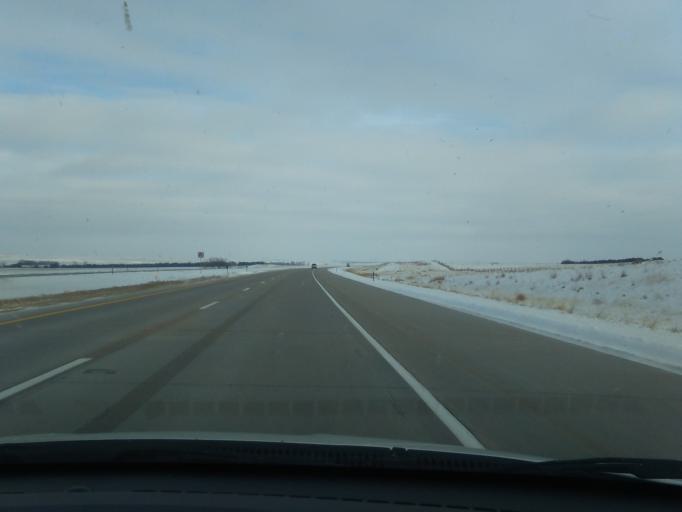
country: US
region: Nebraska
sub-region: Deuel County
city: Chappell
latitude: 41.1125
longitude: -102.5742
